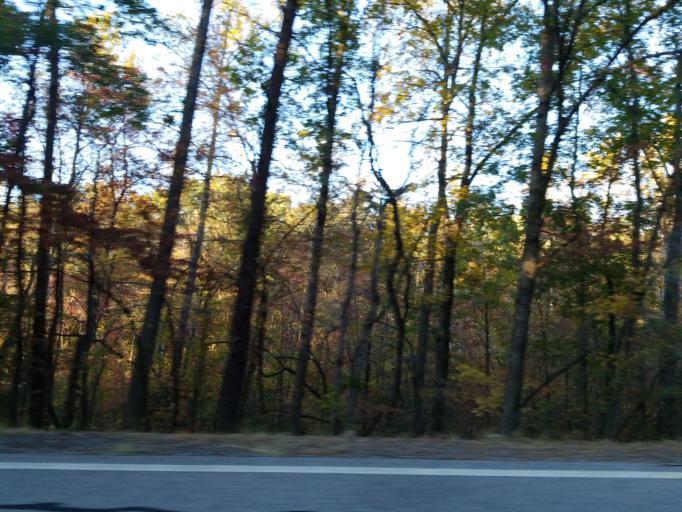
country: US
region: Georgia
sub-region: Dawson County
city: Dawsonville
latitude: 34.5494
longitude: -84.1492
